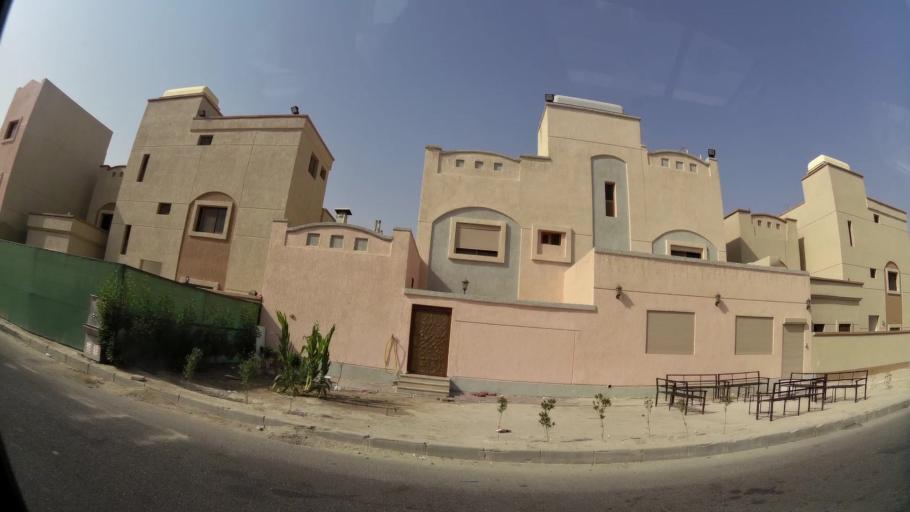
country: KW
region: Muhafazat al Jahra'
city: Al Jahra'
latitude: 29.3479
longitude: 47.7591
